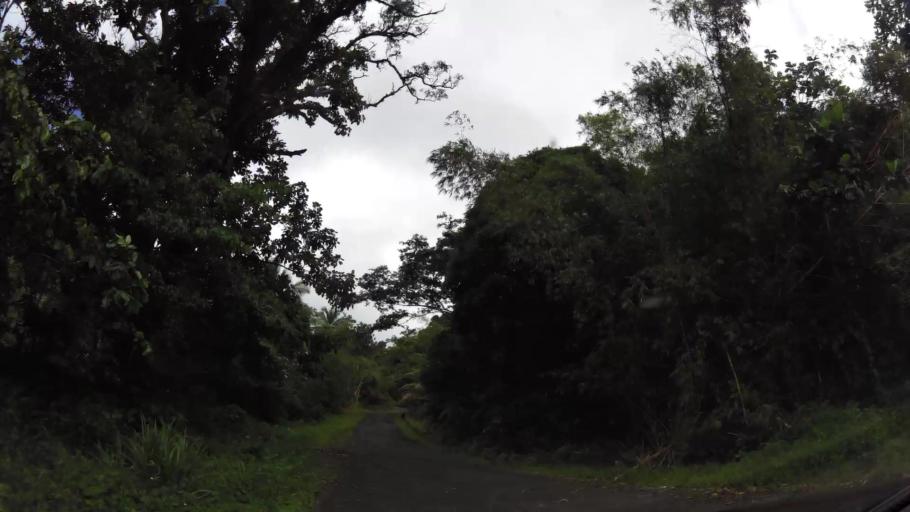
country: DM
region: Saint John
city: Portsmouth
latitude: 15.6113
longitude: -61.4467
